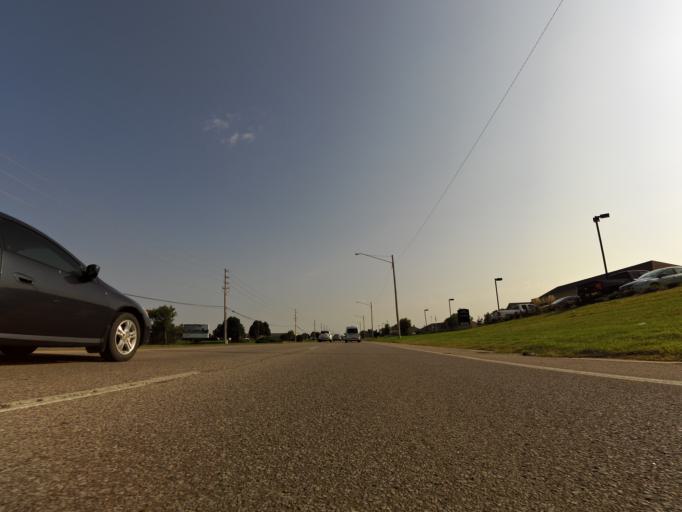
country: US
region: Kansas
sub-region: Sedgwick County
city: Maize
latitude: 37.7497
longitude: -97.4263
